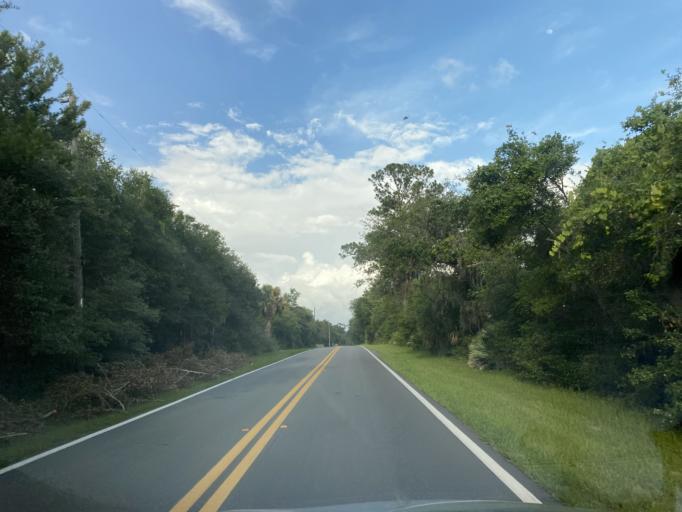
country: US
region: Florida
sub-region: Seminole County
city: Midway
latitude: 28.8454
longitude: -81.1880
